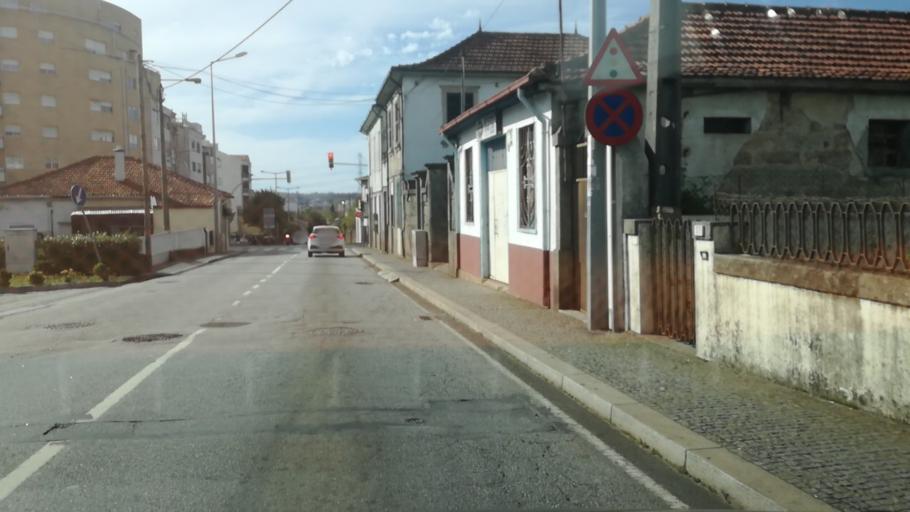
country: PT
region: Porto
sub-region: Maia
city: Nogueira
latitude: 41.2294
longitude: -8.5874
